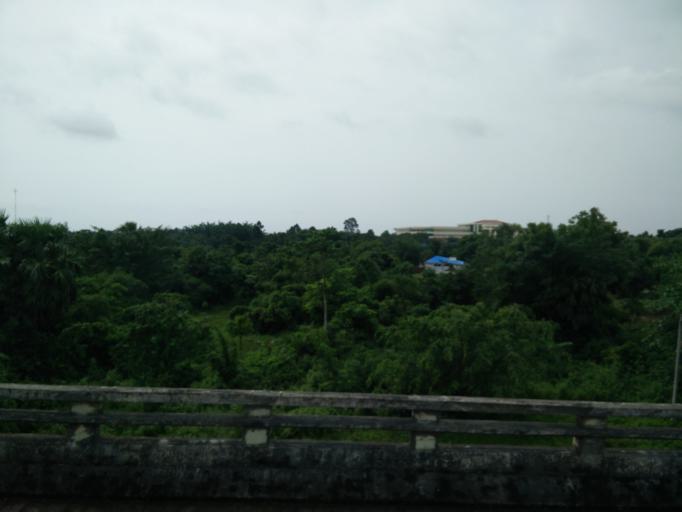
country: MM
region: Ayeyarwady
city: Pathein
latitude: 16.8223
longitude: 94.7306
